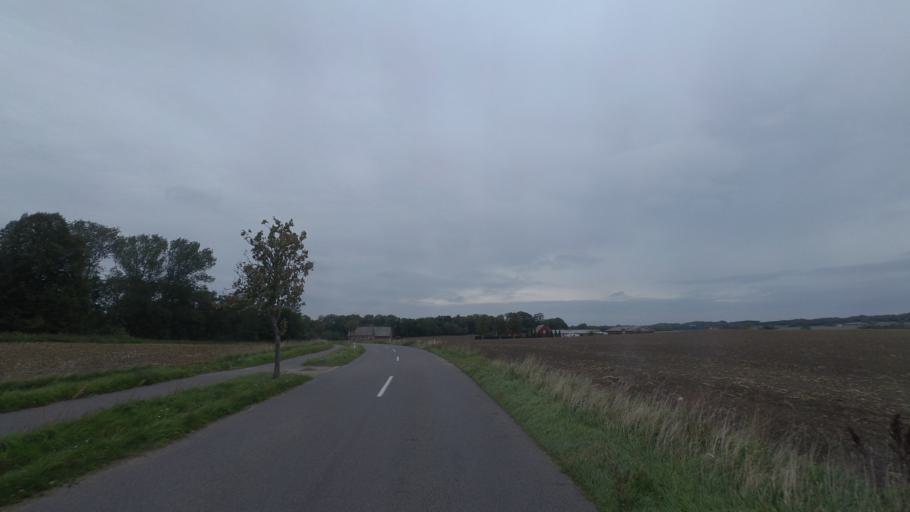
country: DK
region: Capital Region
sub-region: Bornholm Kommune
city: Akirkeby
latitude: 55.0063
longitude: 14.9979
